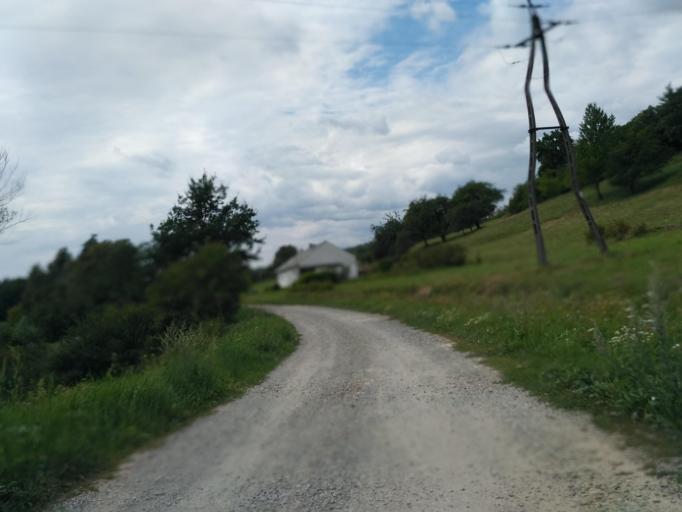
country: PL
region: Subcarpathian Voivodeship
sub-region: Powiat rzeszowski
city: Blazowa
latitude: 49.9383
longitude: 22.0845
